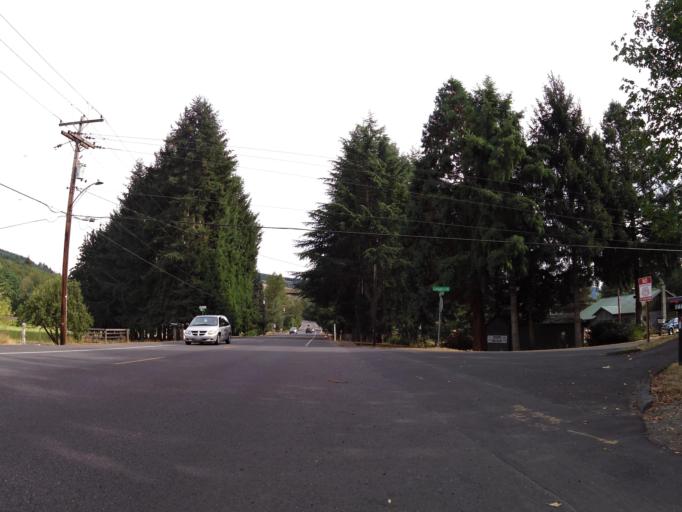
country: US
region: Washington
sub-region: Cowlitz County
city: Castle Rock
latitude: 46.2626
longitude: -122.8957
